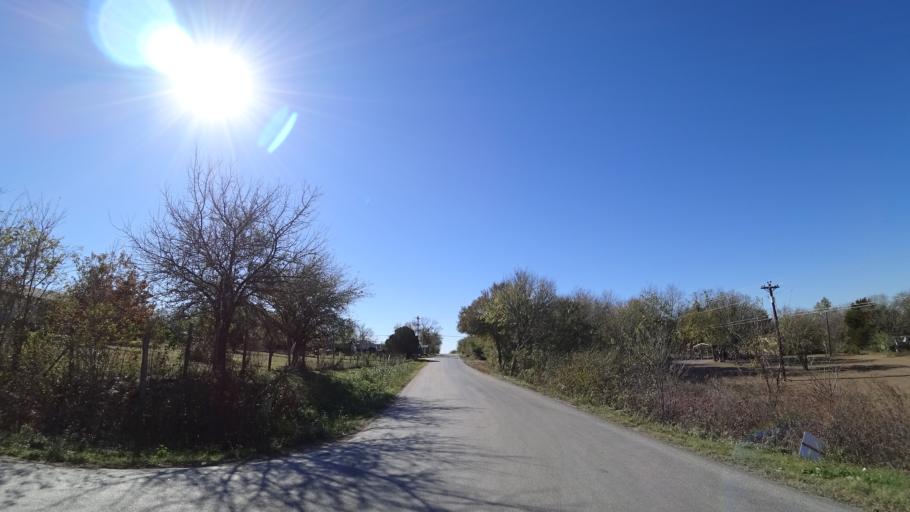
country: US
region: Texas
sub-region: Travis County
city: Garfield
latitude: 30.1108
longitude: -97.5843
